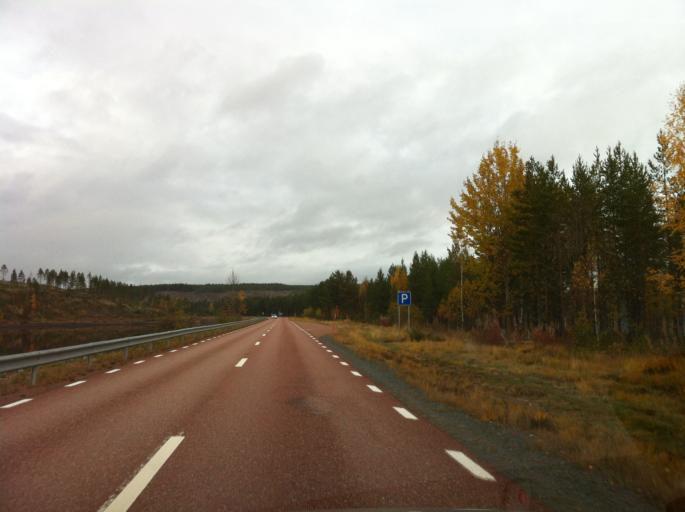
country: SE
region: Dalarna
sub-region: Alvdalens Kommun
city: AElvdalen
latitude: 61.3010
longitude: 13.7280
